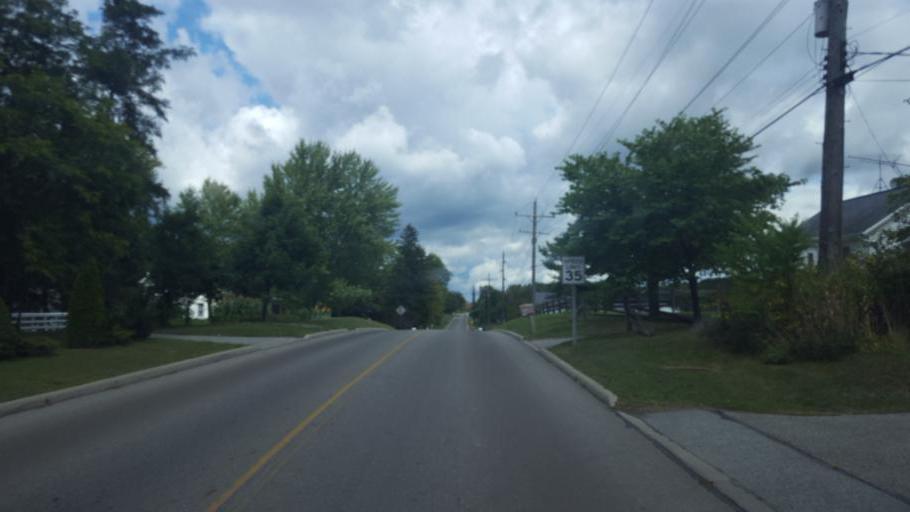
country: US
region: Ohio
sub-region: Geauga County
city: Middlefield
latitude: 41.4495
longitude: -81.0808
